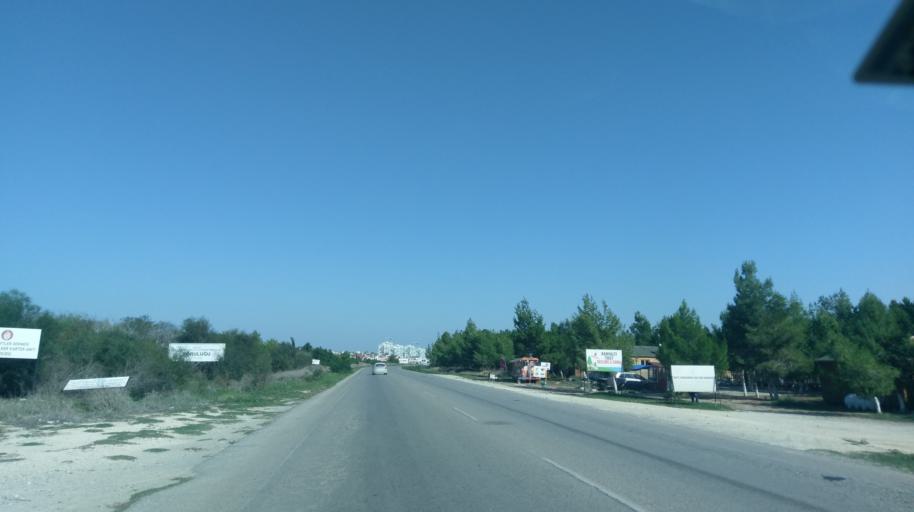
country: CY
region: Ammochostos
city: Trikomo
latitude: 35.2933
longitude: 33.9330
